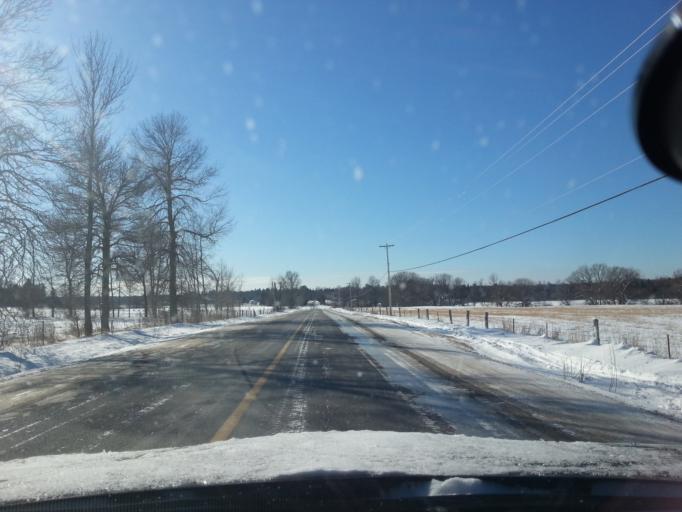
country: CA
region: Ontario
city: Arnprior
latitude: 45.2789
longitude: -76.3045
